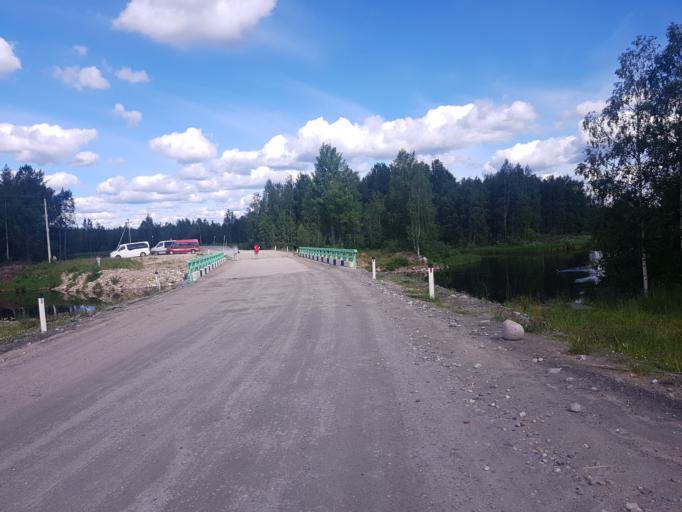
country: RU
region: Republic of Karelia
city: Kostomuksha
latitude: 64.8899
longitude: 30.5283
